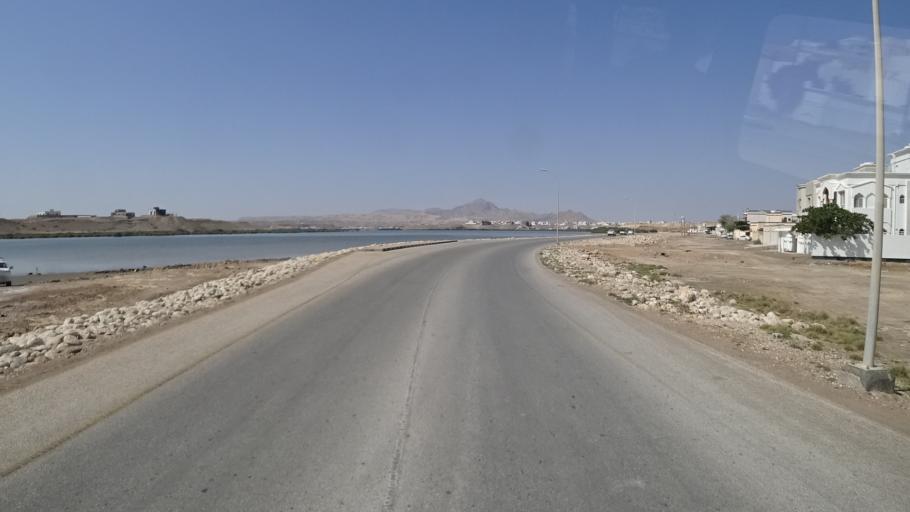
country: OM
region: Ash Sharqiyah
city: Sur
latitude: 22.5711
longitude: 59.5162
